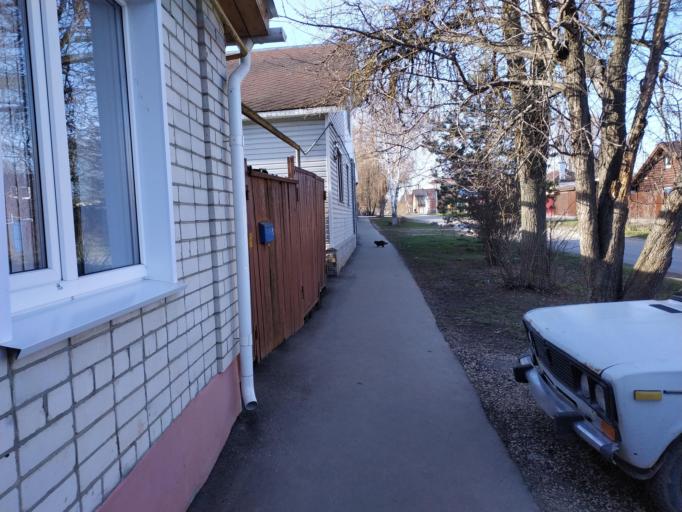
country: RU
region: Nizjnij Novgorod
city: Arzamas
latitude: 55.3976
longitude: 43.8147
